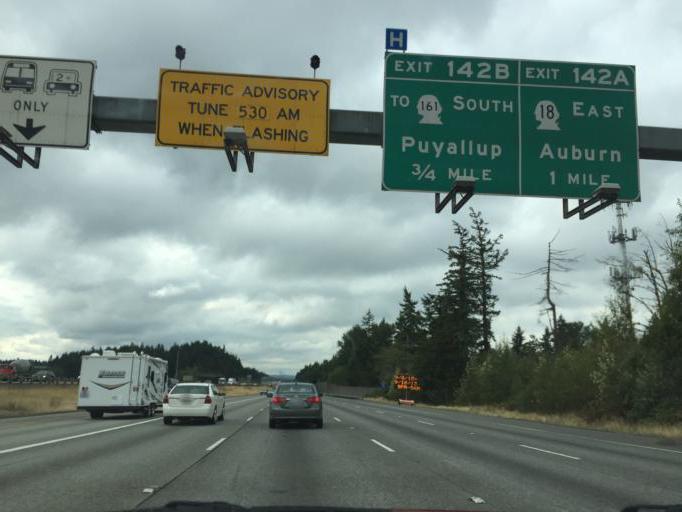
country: US
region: Washington
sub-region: King County
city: Federal Way
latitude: 47.3059
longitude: -122.3014
